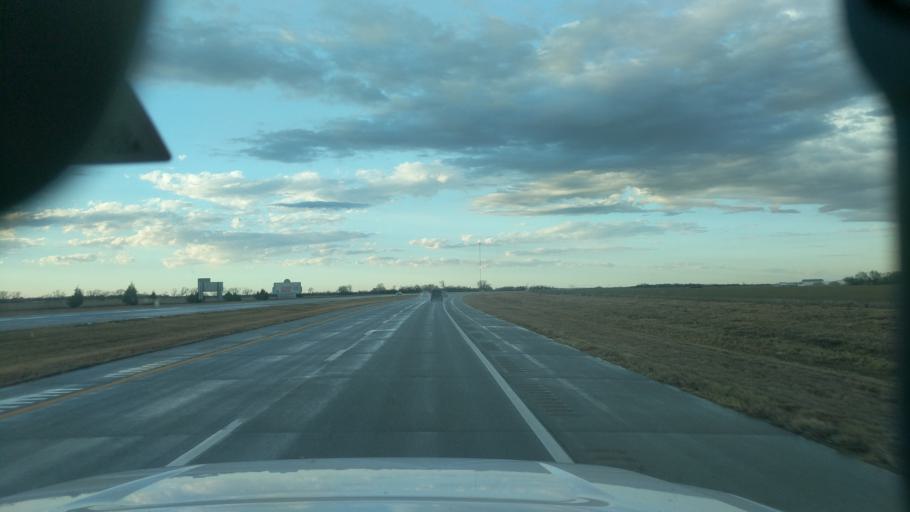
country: US
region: Kansas
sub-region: Harvey County
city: Hesston
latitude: 38.1533
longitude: -97.4275
